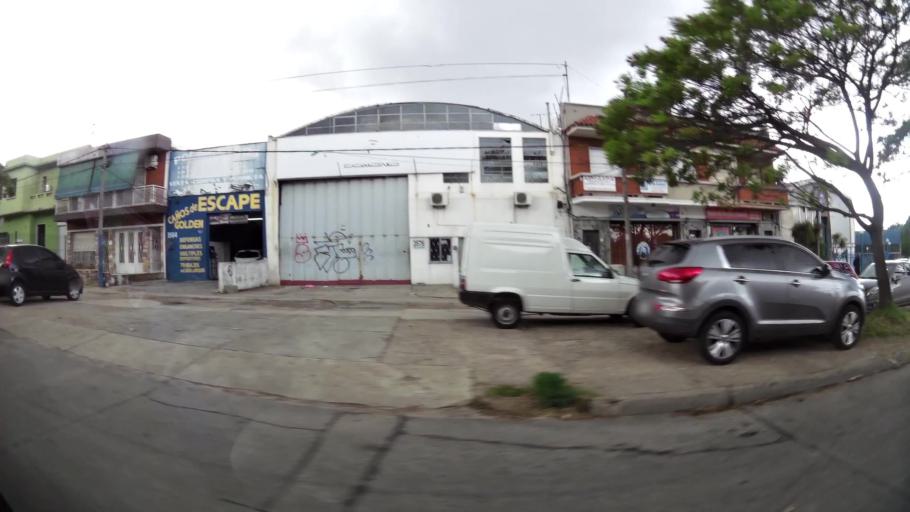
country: UY
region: Montevideo
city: Montevideo
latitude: -34.8620
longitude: -56.1681
